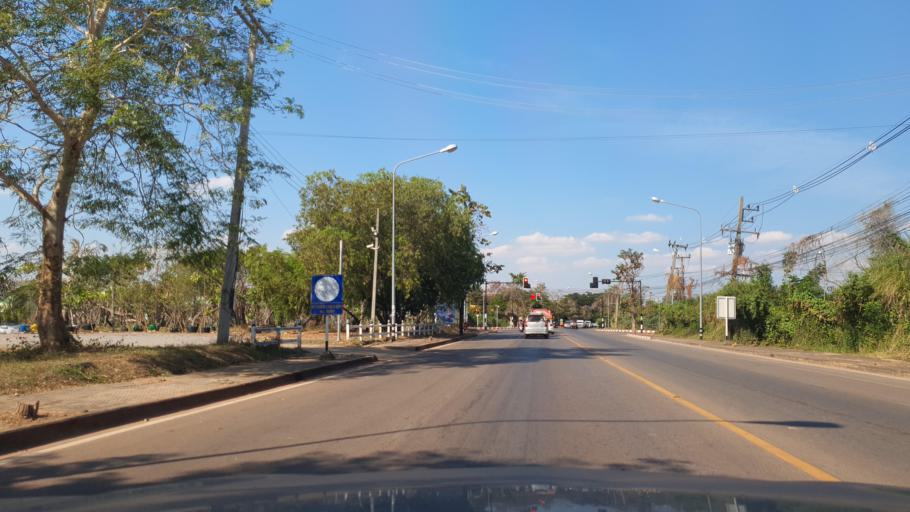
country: TH
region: Sakon Nakhon
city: Sakon Nakhon
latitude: 17.1560
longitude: 104.1265
